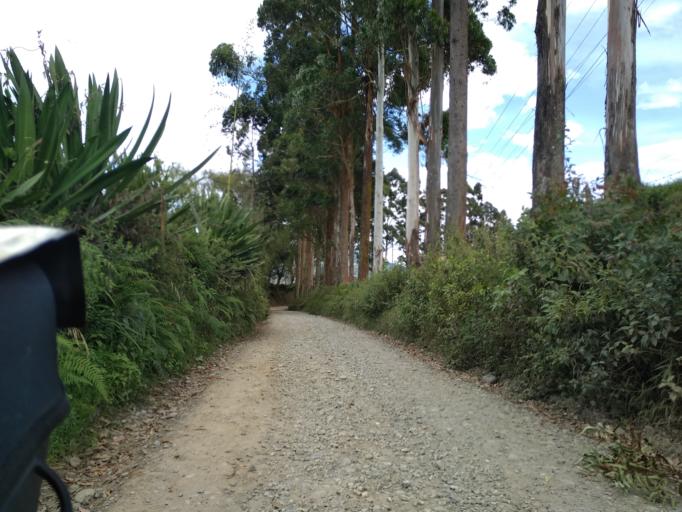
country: CO
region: Quindio
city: Salento
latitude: 4.6328
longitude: -75.5782
